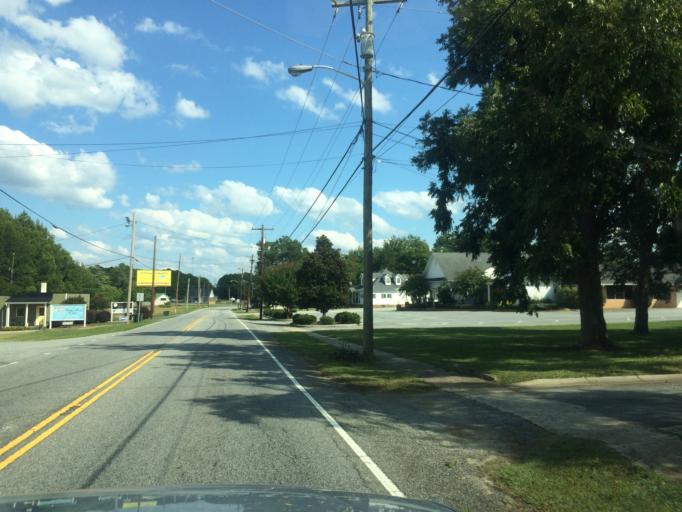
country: US
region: South Carolina
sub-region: Anderson County
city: Honea Path
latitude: 34.4538
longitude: -82.4063
